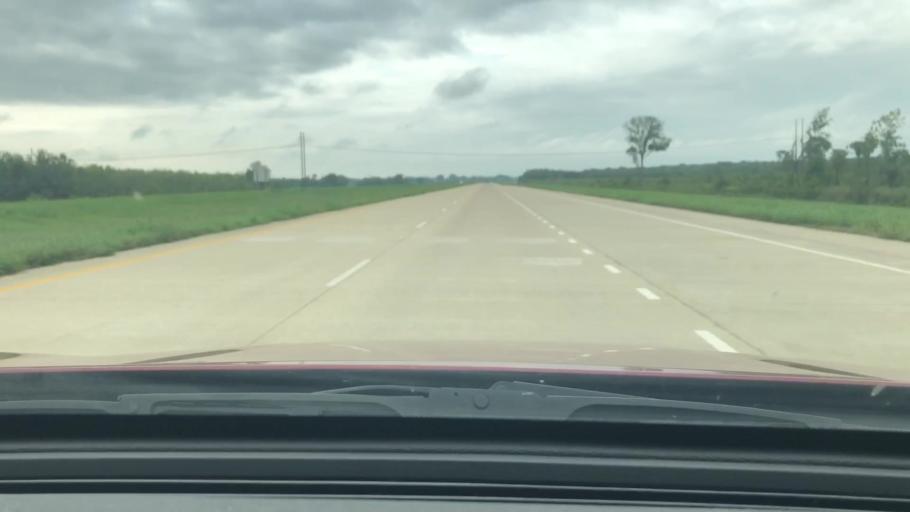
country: US
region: Louisiana
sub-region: Caddo Parish
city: Blanchard
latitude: 32.6708
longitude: -93.8486
